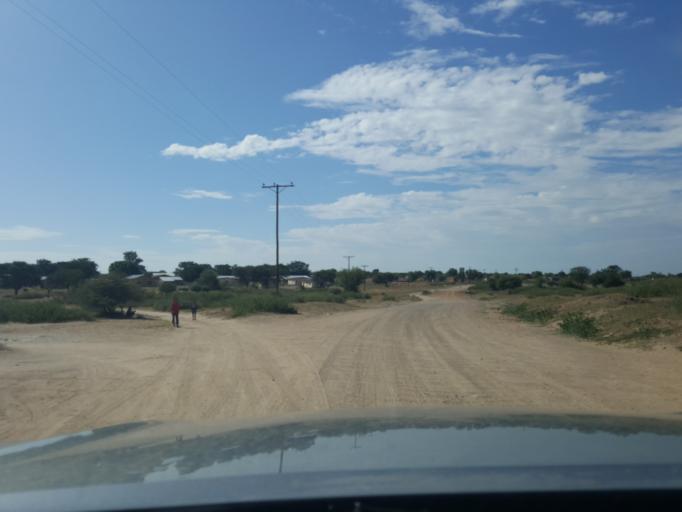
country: BW
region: Kweneng
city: Khudumelapye
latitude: -23.6959
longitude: 24.7174
